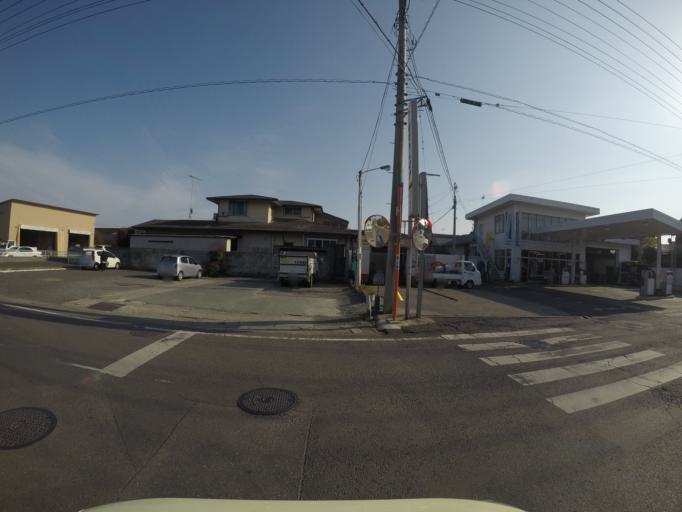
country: JP
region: Ibaraki
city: Ishige
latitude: 36.1457
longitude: 140.0143
